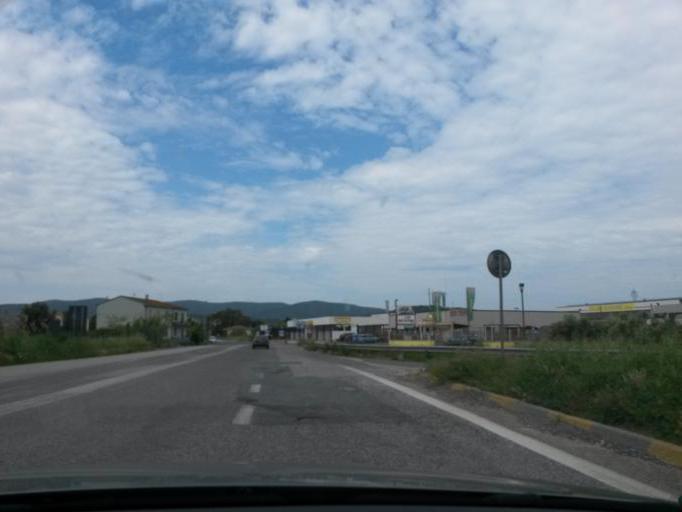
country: IT
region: Tuscany
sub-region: Provincia di Livorno
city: Piombino
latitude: 42.9677
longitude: 10.5532
